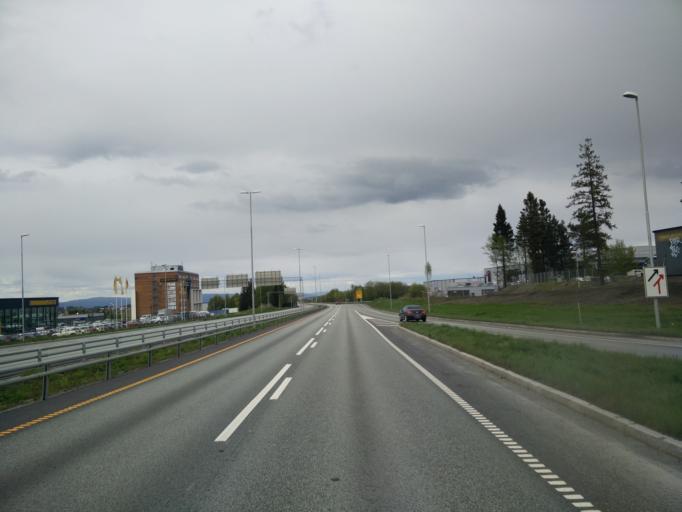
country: NO
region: Sor-Trondelag
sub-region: Trondheim
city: Trondheim
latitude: 63.3648
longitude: 10.3767
